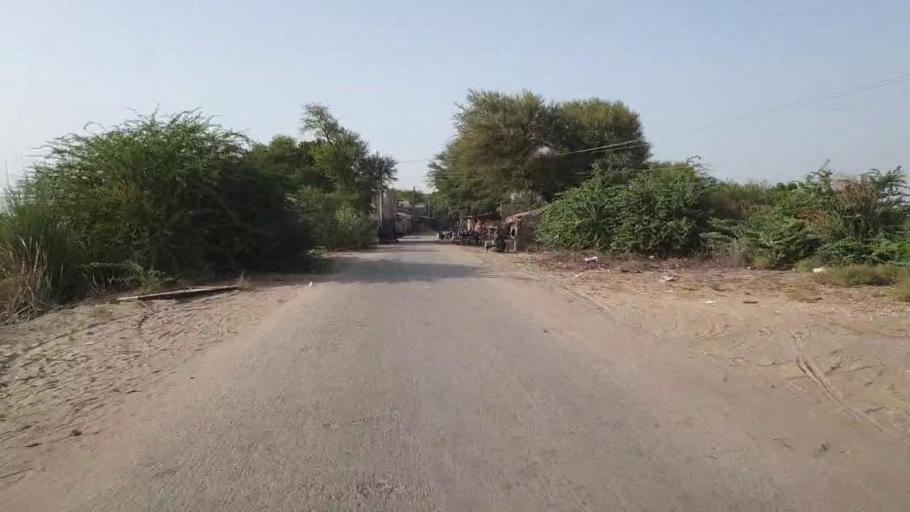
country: PK
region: Sindh
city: Jam Sahib
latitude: 26.4260
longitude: 68.8724
